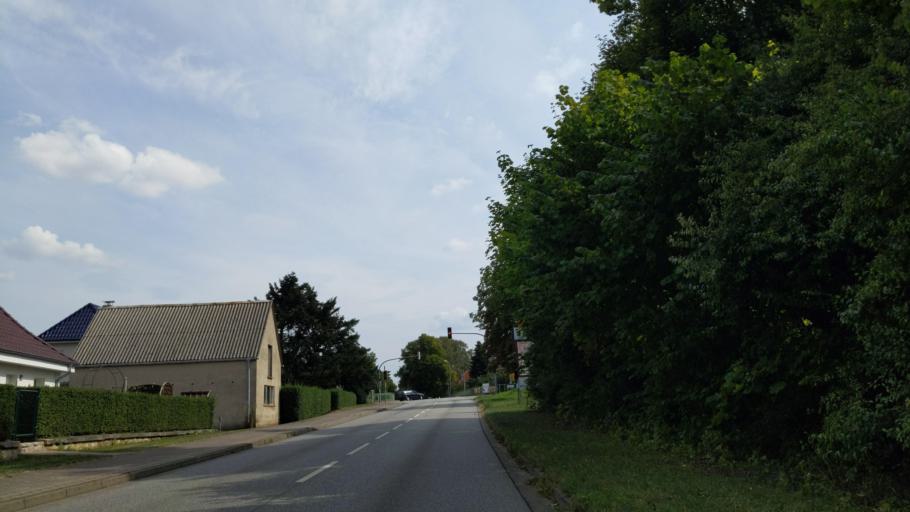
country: DE
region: Mecklenburg-Vorpommern
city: Selmsdorf
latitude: 53.8533
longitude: 10.9229
